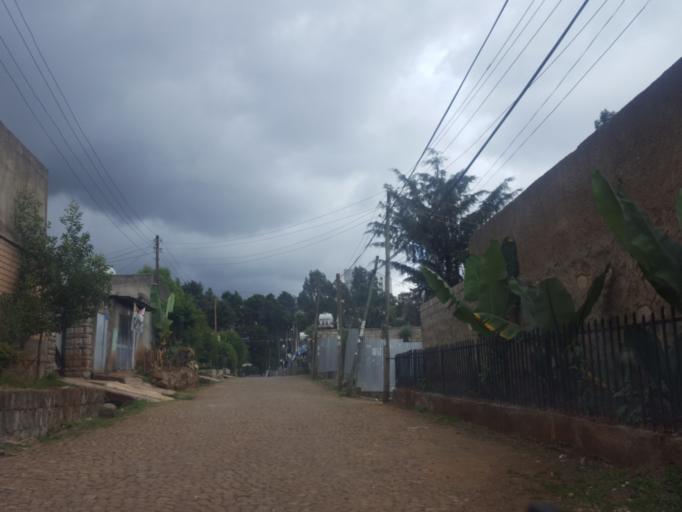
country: ET
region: Adis Abeba
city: Addis Ababa
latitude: 9.0675
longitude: 38.7310
